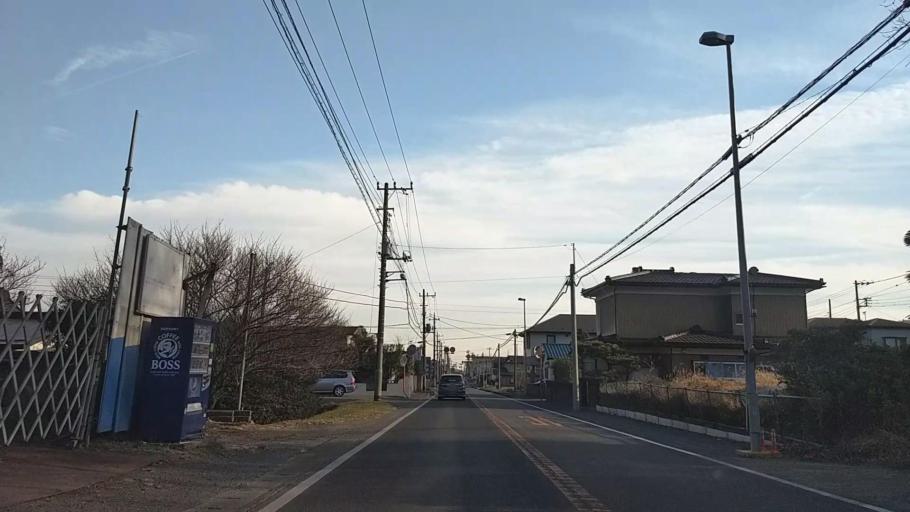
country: JP
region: Kanagawa
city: Zama
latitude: 35.5156
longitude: 139.2974
